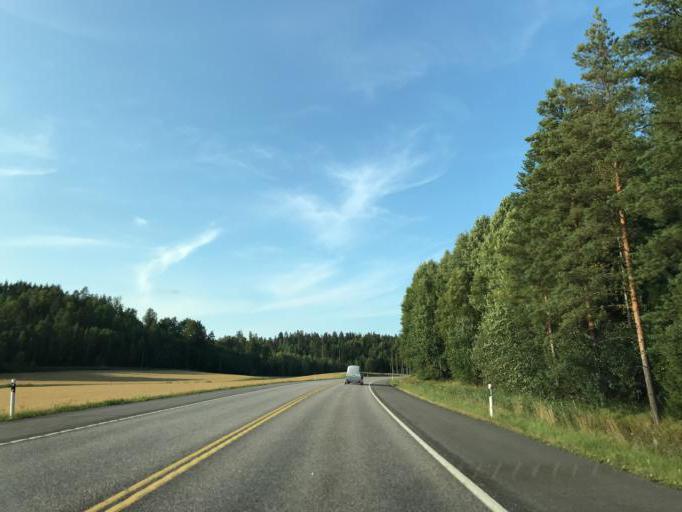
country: FI
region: Uusimaa
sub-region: Helsinki
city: Vihti
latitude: 60.3855
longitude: 24.3177
